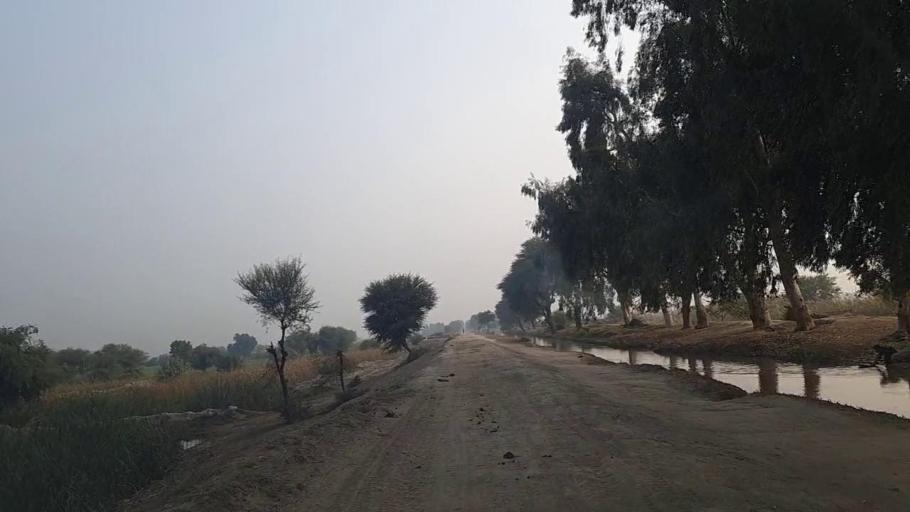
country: PK
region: Sindh
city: Khadro
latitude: 26.1242
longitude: 68.8008
